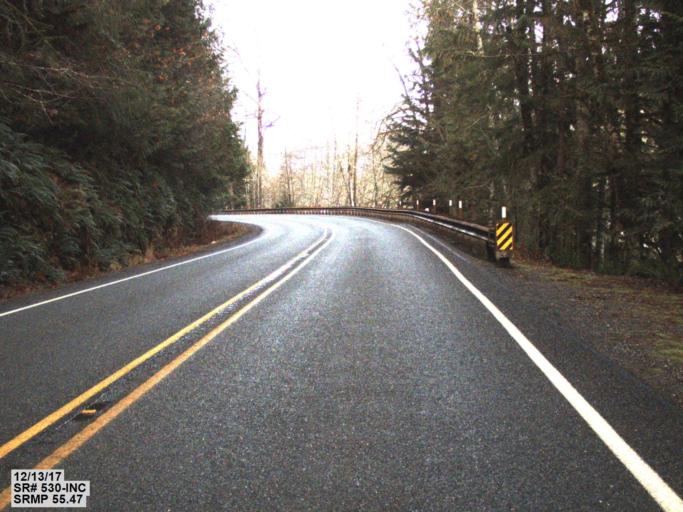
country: US
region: Washington
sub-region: Snohomish County
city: Darrington
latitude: 48.3351
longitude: -121.5498
